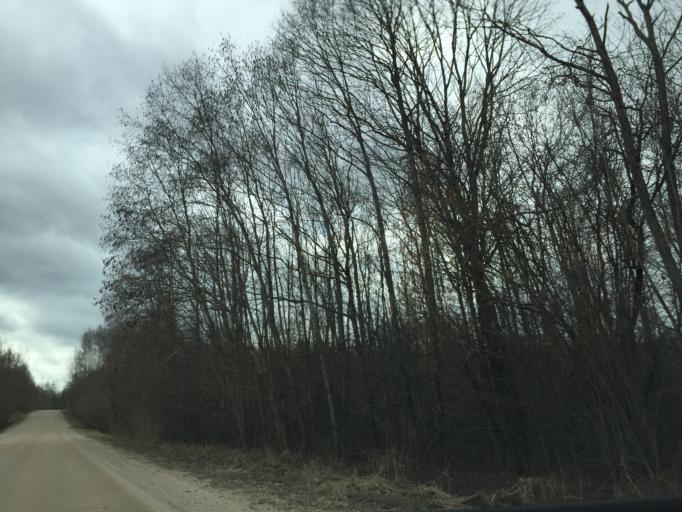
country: LV
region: Kraslavas Rajons
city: Kraslava
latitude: 55.9478
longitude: 26.9966
